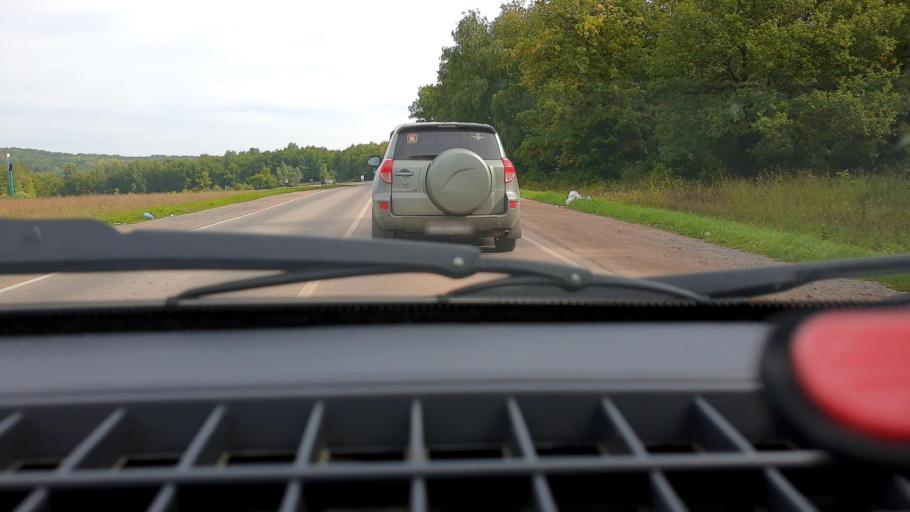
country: RU
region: Bashkortostan
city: Avdon
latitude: 54.6390
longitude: 55.6071
